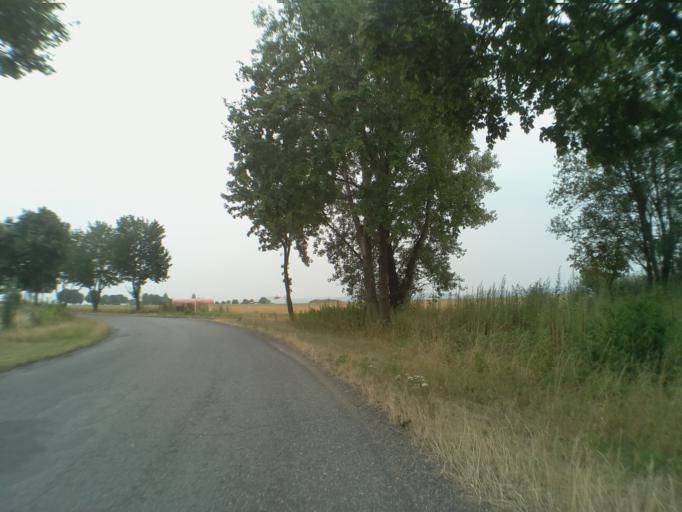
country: PL
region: Lower Silesian Voivodeship
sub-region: Powiat swidnicki
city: Swiebodzice
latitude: 50.8864
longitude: 16.3213
